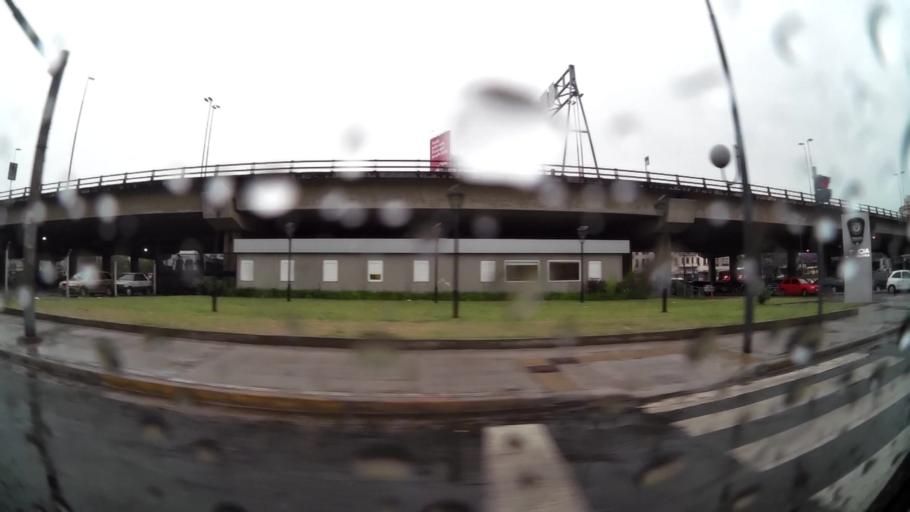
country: AR
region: Buenos Aires F.D.
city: Buenos Aires
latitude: -34.6272
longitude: -58.3798
